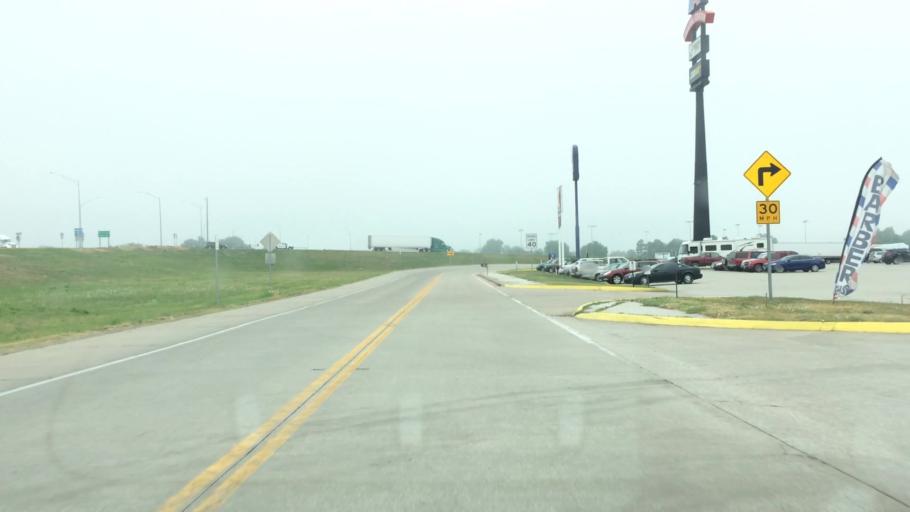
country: US
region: Missouri
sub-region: Greene County
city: Strafford
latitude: 37.2753
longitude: -93.1143
